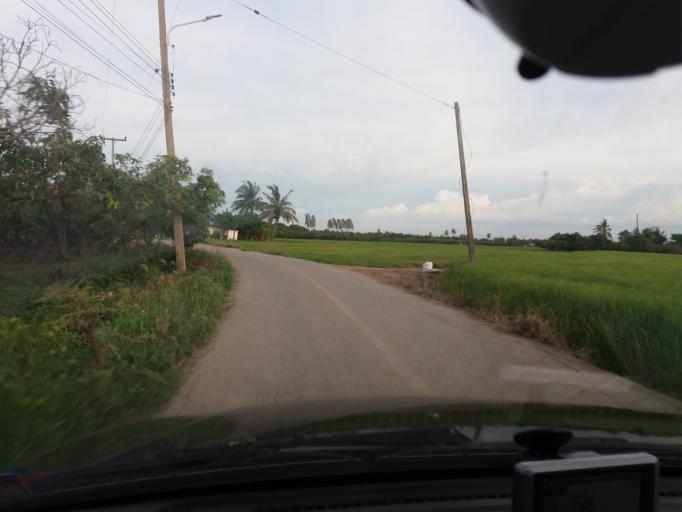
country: TH
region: Suphan Buri
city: Doembang Nangbuat
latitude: 14.8121
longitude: 100.1396
